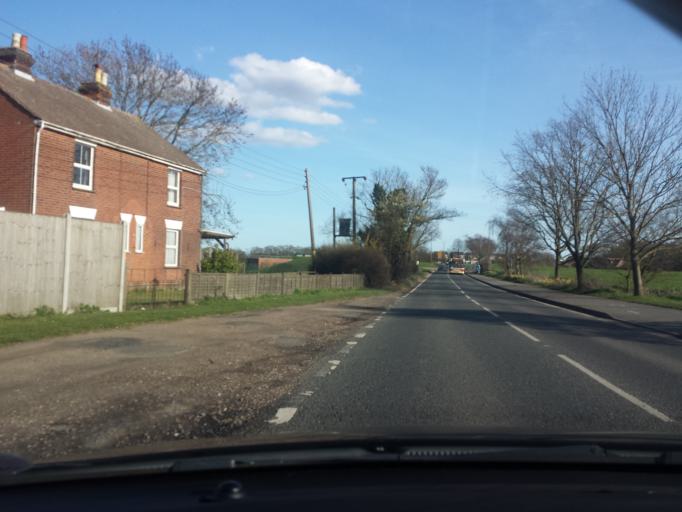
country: GB
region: England
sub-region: Essex
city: Brightlingsea
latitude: 51.8274
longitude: 1.0150
